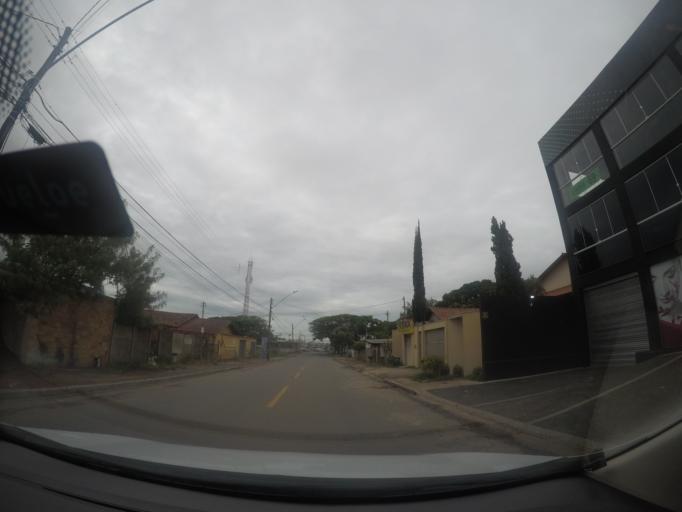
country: BR
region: Goias
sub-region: Goiania
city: Goiania
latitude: -16.6547
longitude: -49.3161
